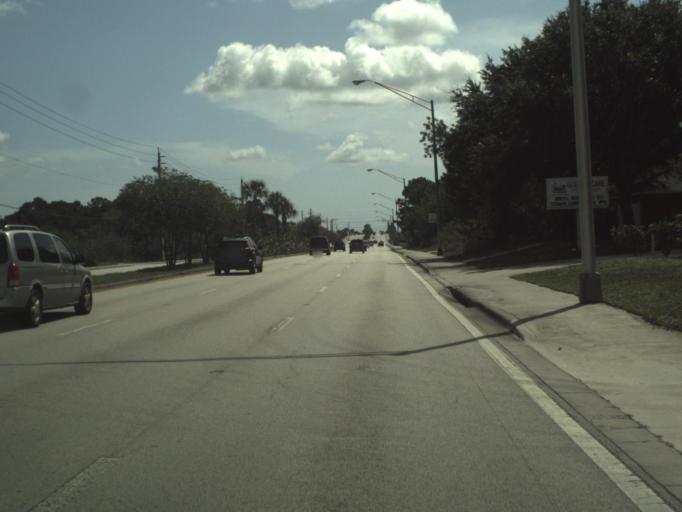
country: US
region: Florida
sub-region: Saint Lucie County
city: Port Saint Lucie
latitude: 27.2692
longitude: -80.3667
